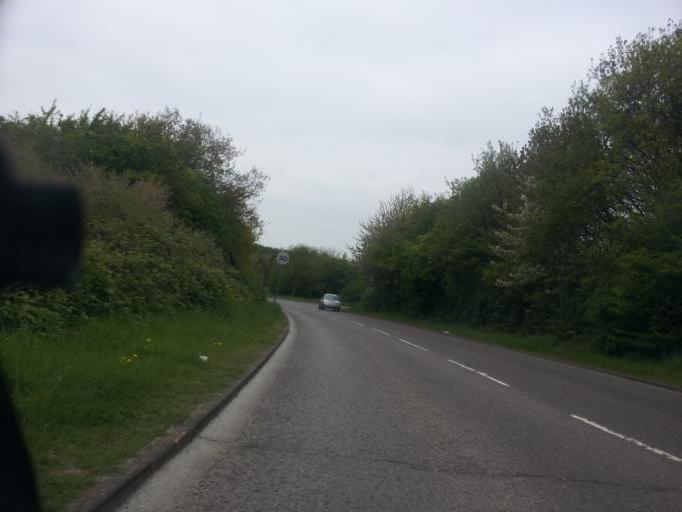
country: GB
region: England
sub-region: Medway
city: Rochester
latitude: 51.4146
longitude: 0.5228
